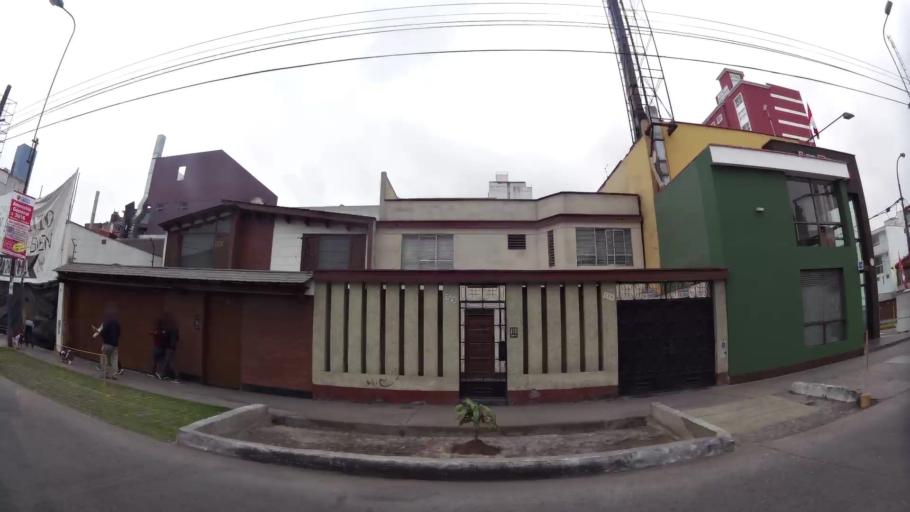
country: PE
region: Lima
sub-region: Lima
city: Surco
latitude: -12.1208
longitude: -77.0039
